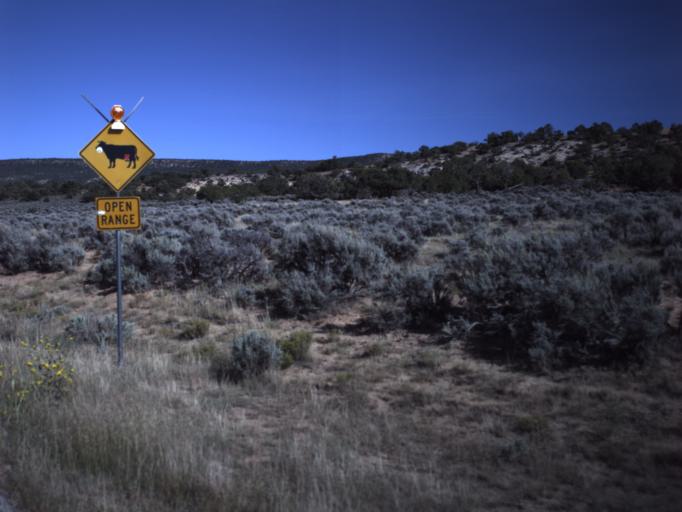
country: US
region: Utah
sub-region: San Juan County
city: Monticello
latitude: 38.0006
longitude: -109.4651
